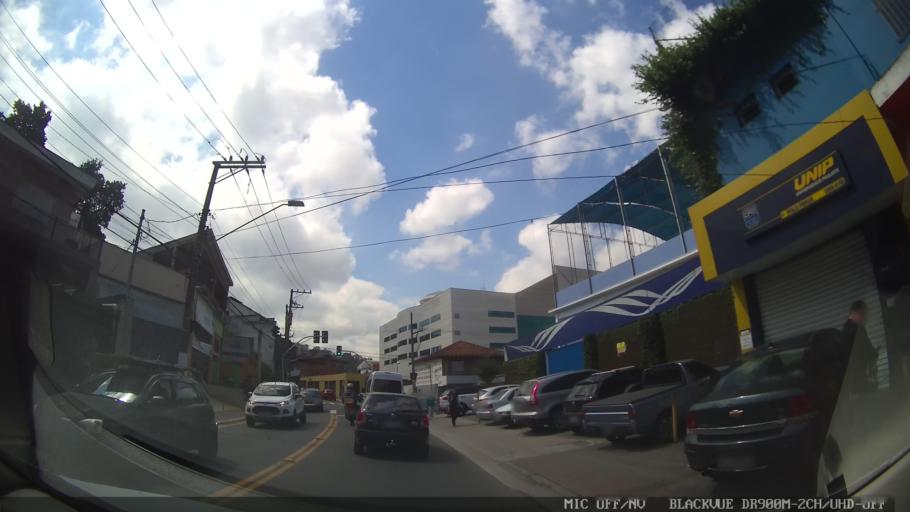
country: BR
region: Sao Paulo
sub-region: Caieiras
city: Caieiras
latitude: -23.4047
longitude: -46.7498
